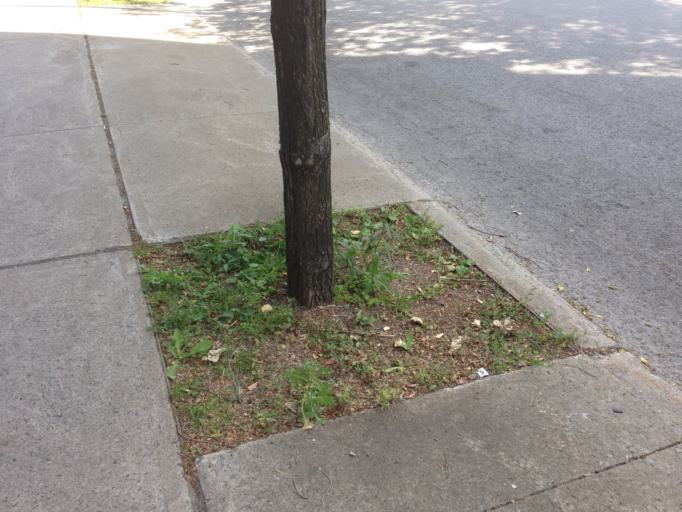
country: CA
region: Quebec
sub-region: Monteregie
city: Longueuil
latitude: 45.5219
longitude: -73.5510
